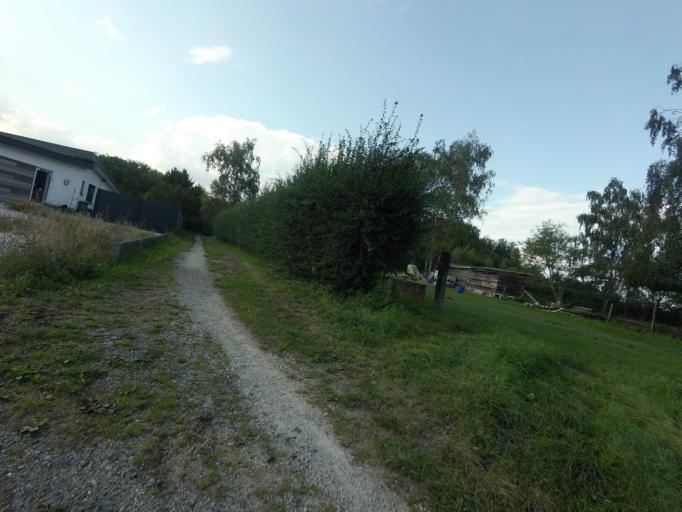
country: BE
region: Flanders
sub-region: Provincie Vlaams-Brabant
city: Boortmeerbeek
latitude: 50.9832
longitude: 4.5610
